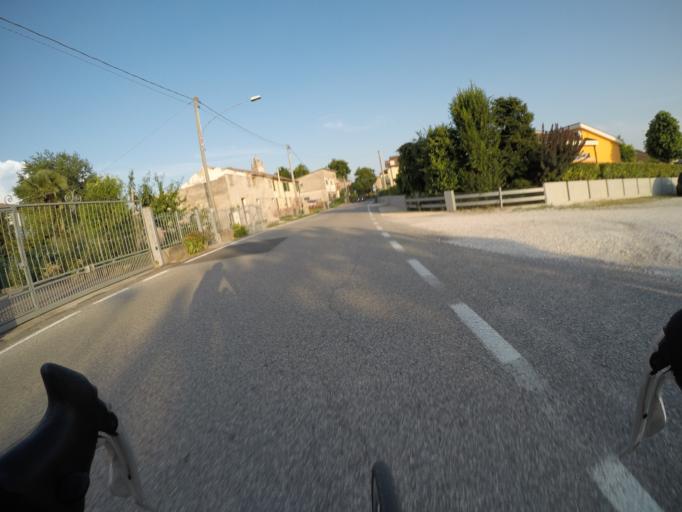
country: IT
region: Veneto
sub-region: Provincia di Rovigo
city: Villanova del Ghebbo Canton
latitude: 45.0565
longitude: 11.6423
